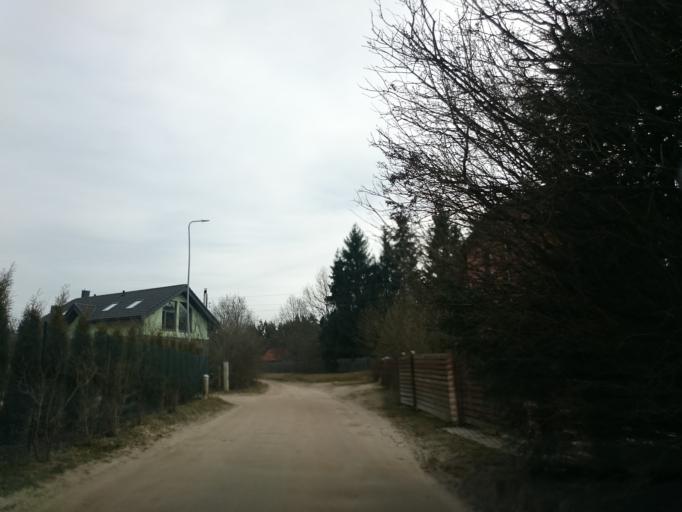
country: LV
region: Garkalne
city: Garkalne
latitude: 57.0153
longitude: 24.3932
